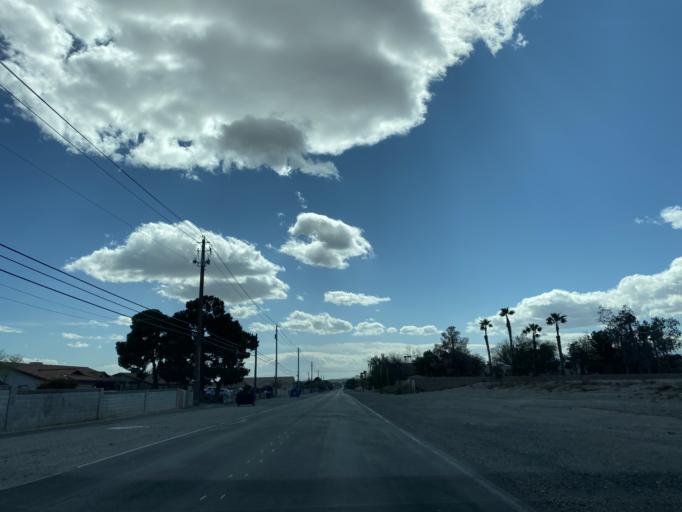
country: US
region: Nevada
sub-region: Clark County
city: Summerlin South
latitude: 36.2591
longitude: -115.2885
